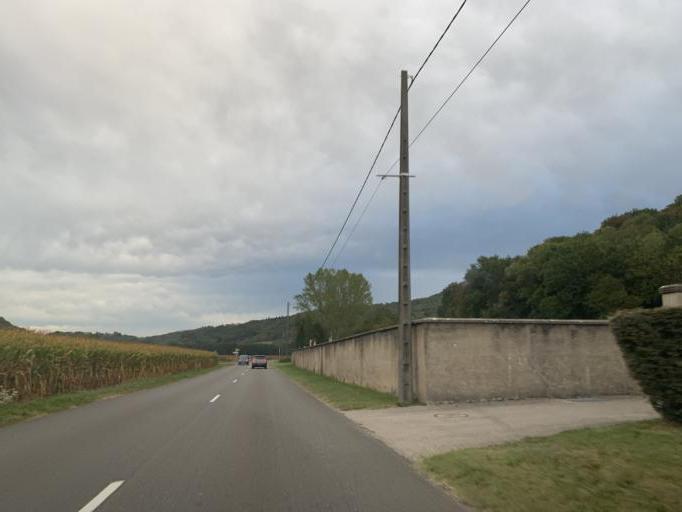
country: FR
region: Rhone-Alpes
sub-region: Departement de l'Ain
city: Belley
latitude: 45.7125
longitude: 5.6613
